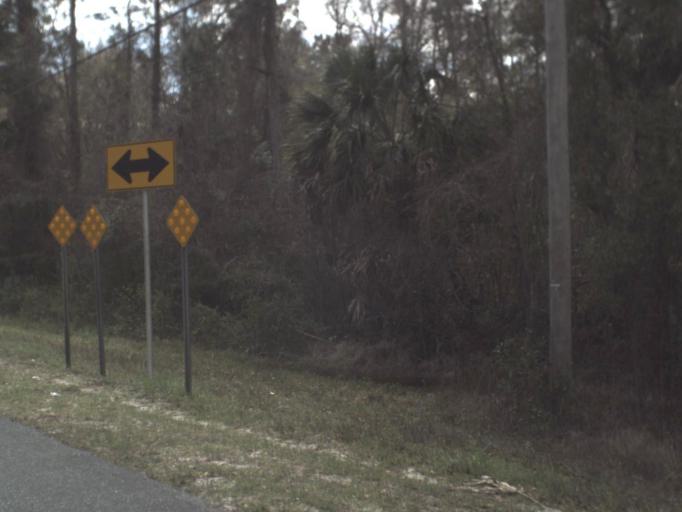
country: US
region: Florida
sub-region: Wakulla County
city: Crawfordville
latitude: 30.0934
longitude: -84.3856
